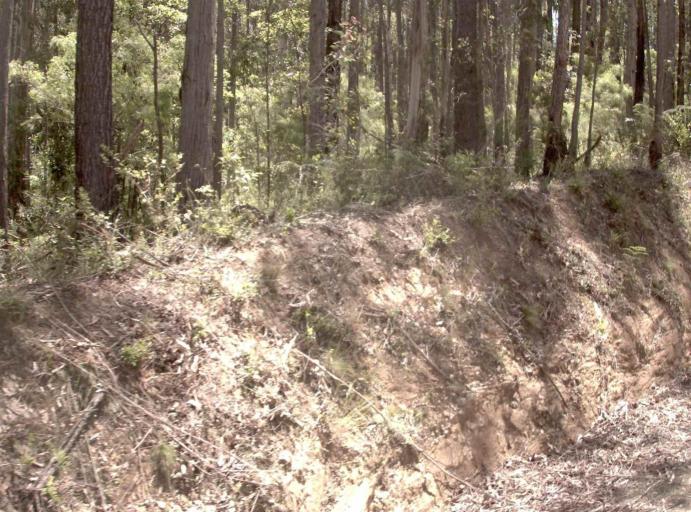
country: AU
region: New South Wales
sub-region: Bombala
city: Bombala
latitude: -37.5776
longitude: 148.9392
